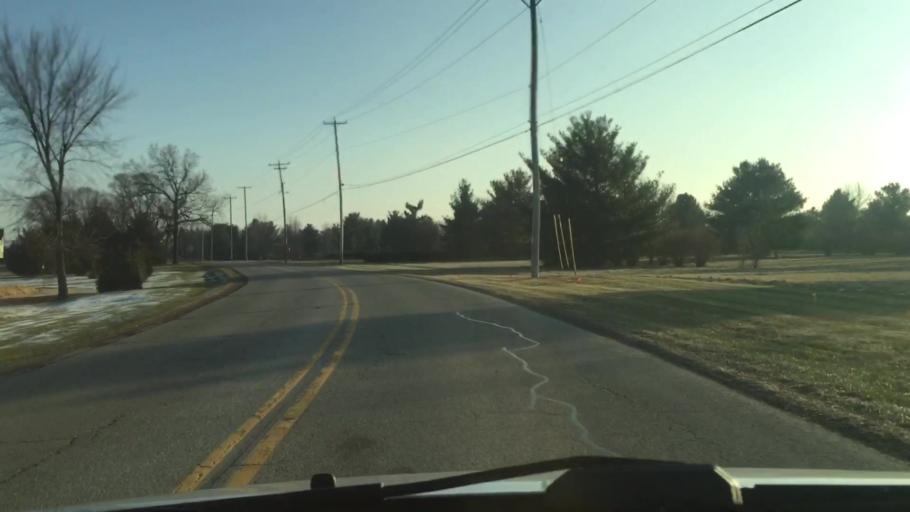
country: US
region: Wisconsin
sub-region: Waukesha County
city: Dousman
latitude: 43.0438
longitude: -88.4871
